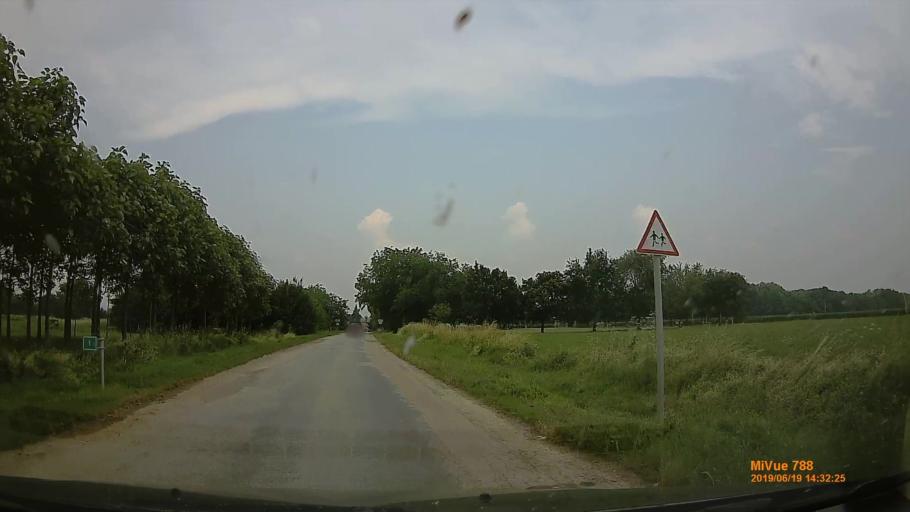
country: HU
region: Baranya
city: Szigetvar
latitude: 46.0730
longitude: 17.7772
